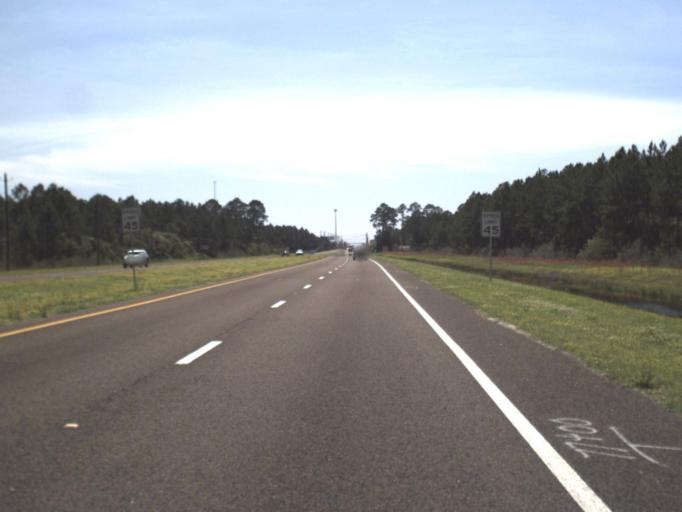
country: US
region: Florida
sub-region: Bay County
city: Laguna Beach
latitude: 30.2396
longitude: -85.8838
